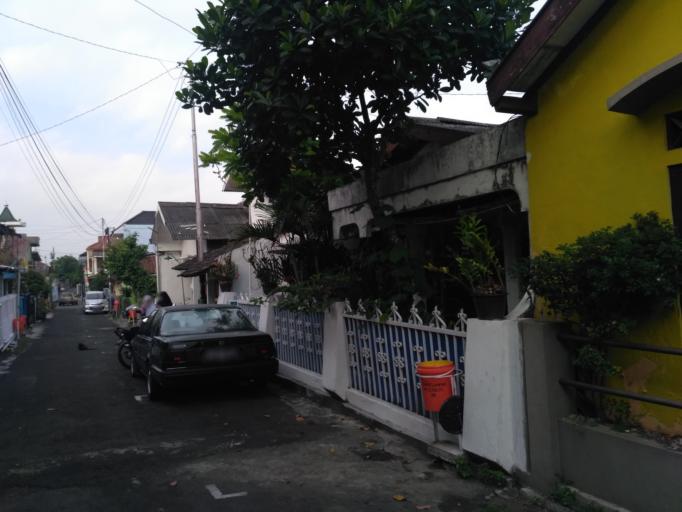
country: ID
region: Daerah Istimewa Yogyakarta
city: Melati
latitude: -7.7372
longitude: 110.3873
